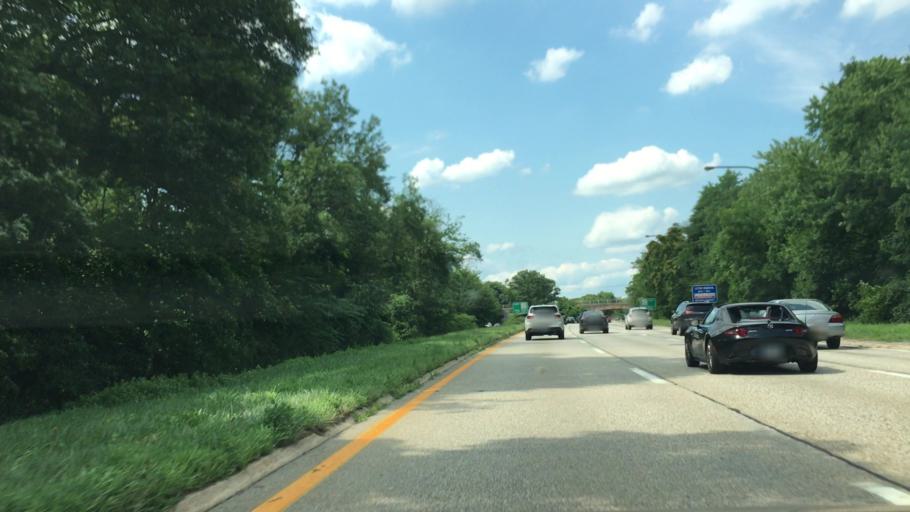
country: US
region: New York
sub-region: Nassau County
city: North Merrick
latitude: 40.6771
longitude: -73.5716
